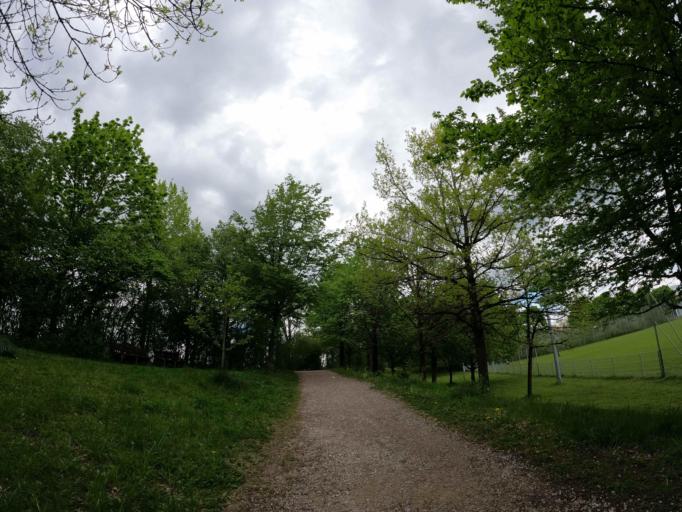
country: DE
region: Bavaria
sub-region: Upper Bavaria
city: Haar
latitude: 48.1136
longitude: 11.7256
